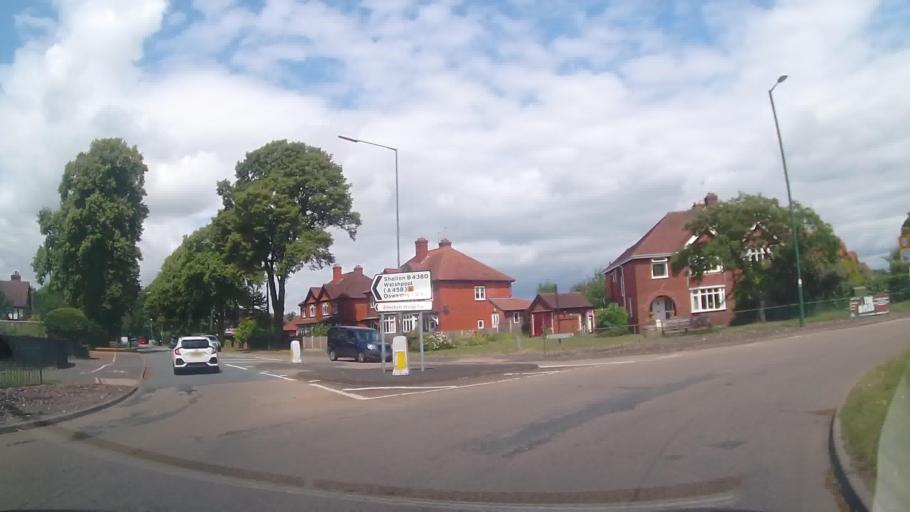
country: GB
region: England
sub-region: Shropshire
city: Shrewsbury
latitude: 52.7079
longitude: -2.7793
